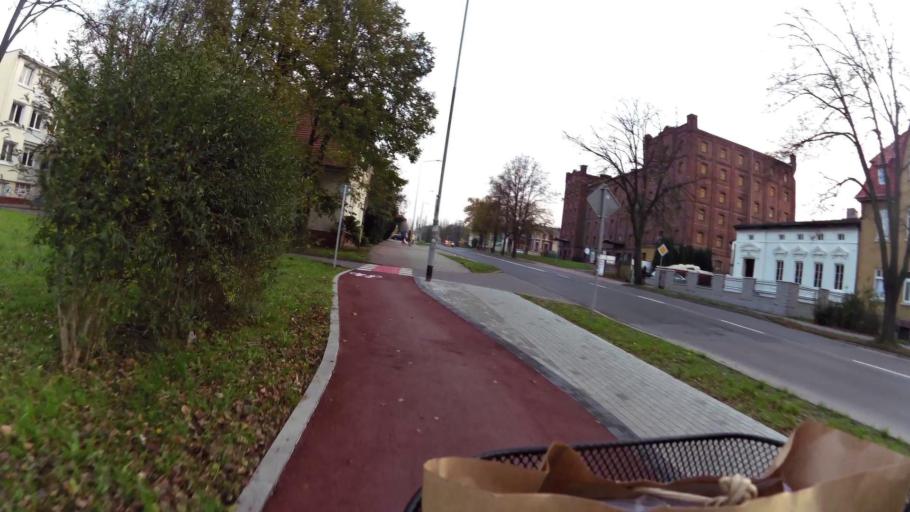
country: PL
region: West Pomeranian Voivodeship
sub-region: Koszalin
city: Koszalin
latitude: 54.1968
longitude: 16.1671
